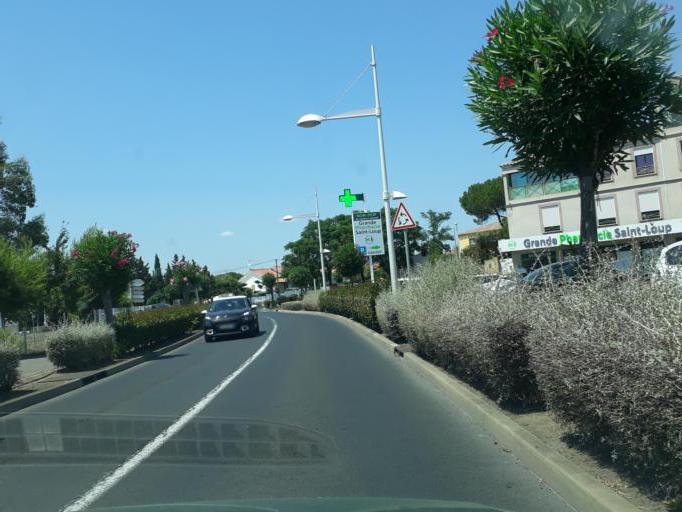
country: FR
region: Languedoc-Roussillon
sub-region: Departement de l'Herault
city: Agde
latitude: 43.3010
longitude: 3.4712
